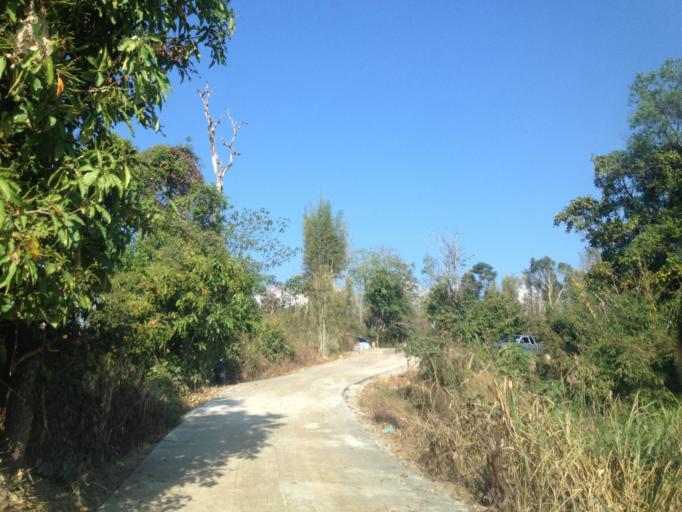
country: TH
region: Mae Hong Son
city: Ban Huai I Huak
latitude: 18.1106
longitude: 98.2091
